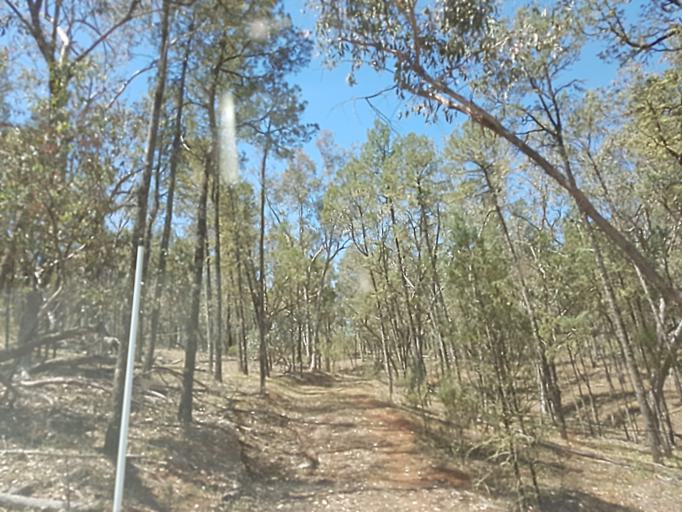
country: AU
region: New South Wales
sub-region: Snowy River
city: Jindabyne
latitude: -36.9419
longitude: 148.3877
